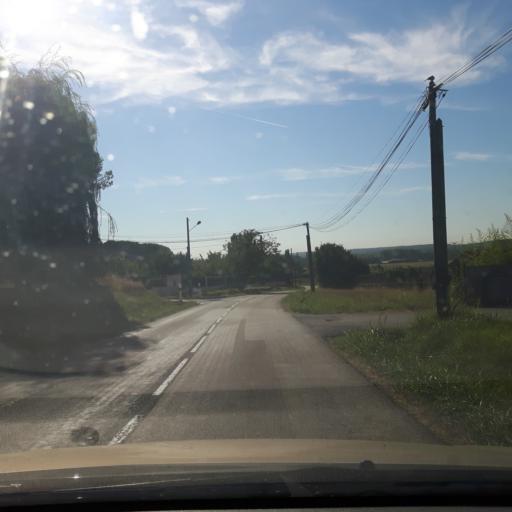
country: FR
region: Midi-Pyrenees
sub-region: Departement de la Haute-Garonne
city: Bouloc
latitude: 43.7688
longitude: 1.3969
